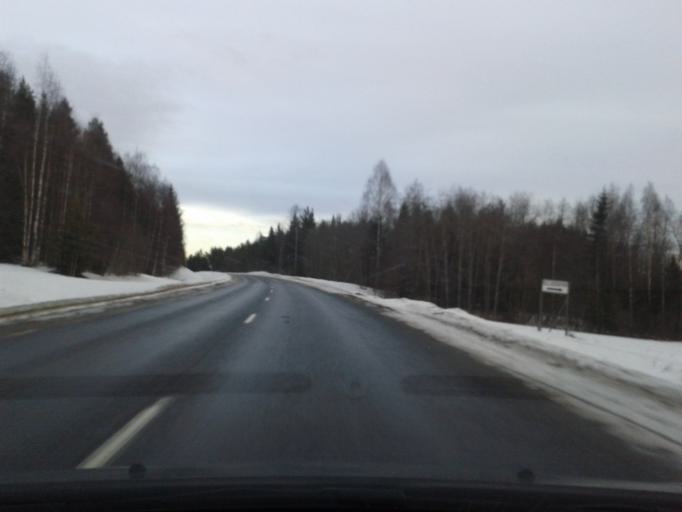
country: SE
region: Vaesternorrland
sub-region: Solleftea Kommun
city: Solleftea
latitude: 63.3342
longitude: 17.0894
